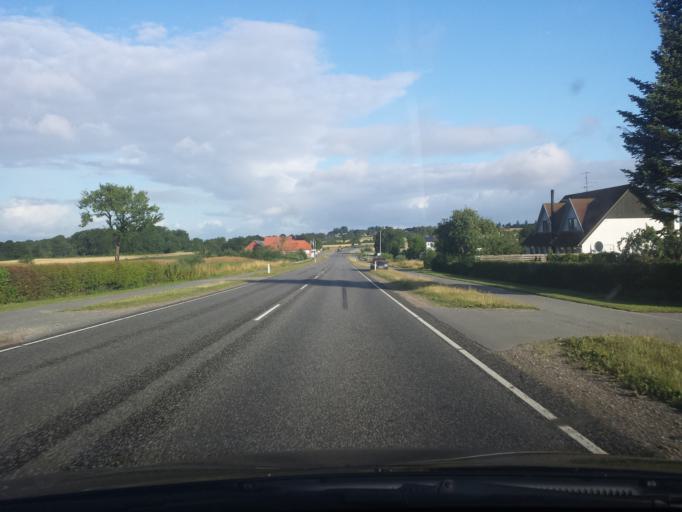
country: DK
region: South Denmark
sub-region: Sonderborg Kommune
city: Guderup
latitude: 54.9750
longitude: 9.8900
